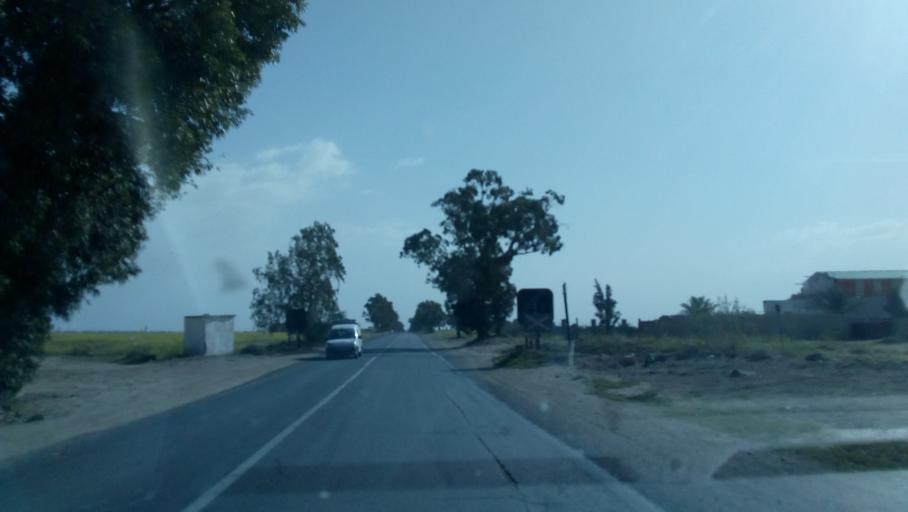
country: TN
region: Qabis
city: Gabes
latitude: 33.8923
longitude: 10.0383
